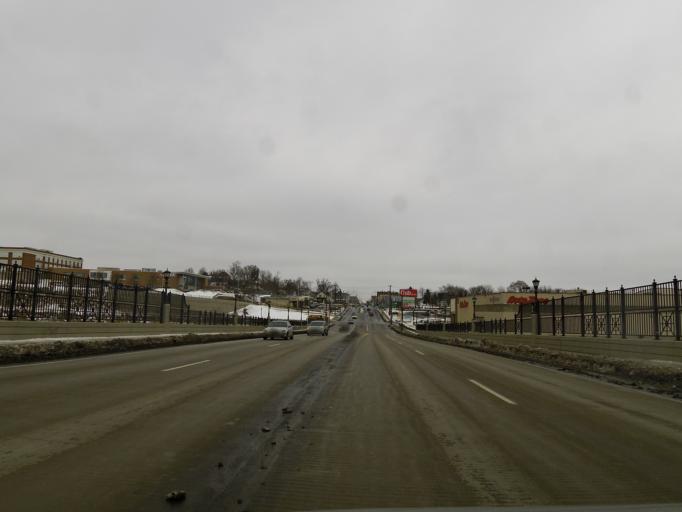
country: US
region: Minnesota
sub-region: Ramsey County
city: Saint Paul
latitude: 44.9656
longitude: -93.0660
